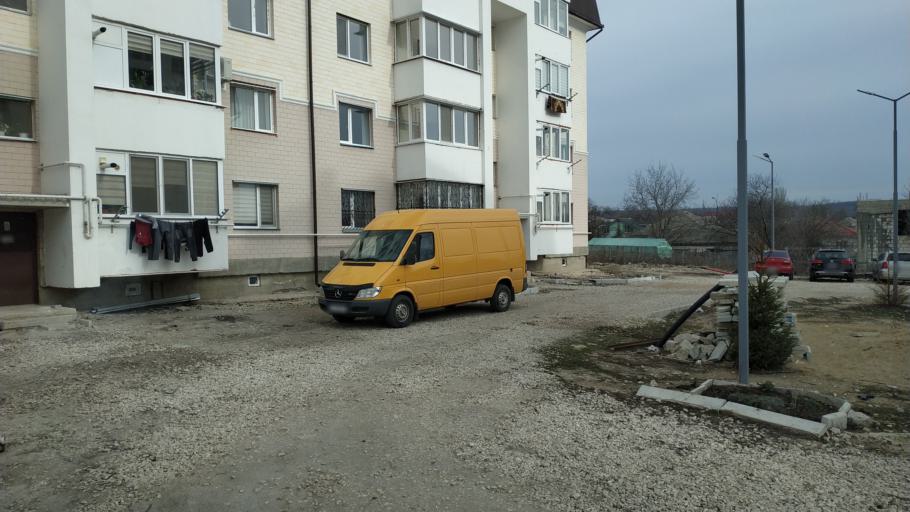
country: MD
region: Chisinau
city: Vatra
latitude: 47.0924
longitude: 28.7617
